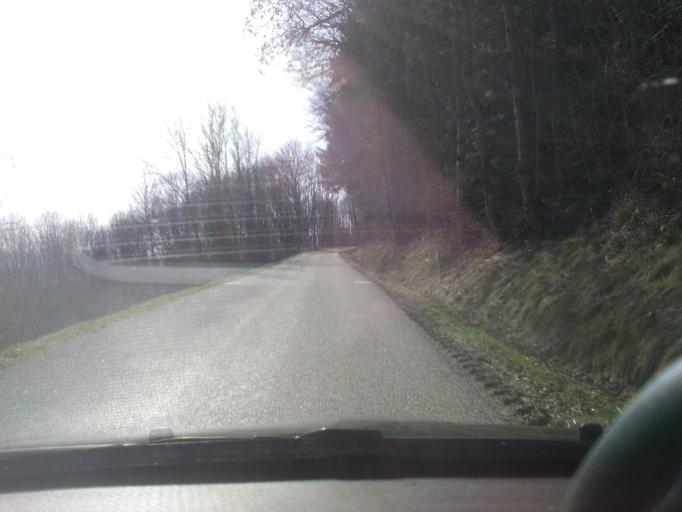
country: FR
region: Lorraine
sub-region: Departement des Vosges
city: Ban-de-Laveline
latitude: 48.3451
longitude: 7.0934
